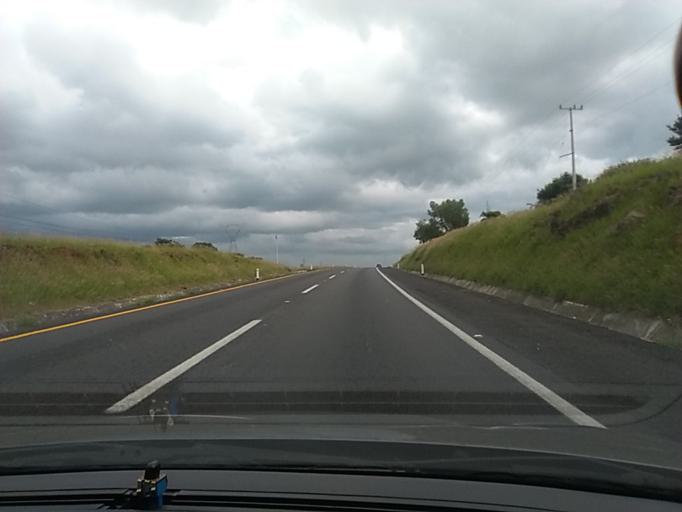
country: MX
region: Jalisco
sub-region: Zapotlanejo
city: La Mezquitera
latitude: 20.5993
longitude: -103.1163
